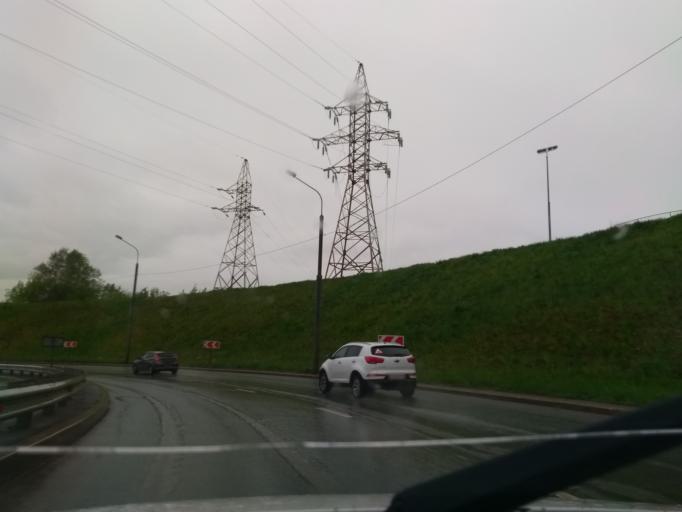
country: RU
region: Perm
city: Perm
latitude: 58.0088
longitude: 56.3214
